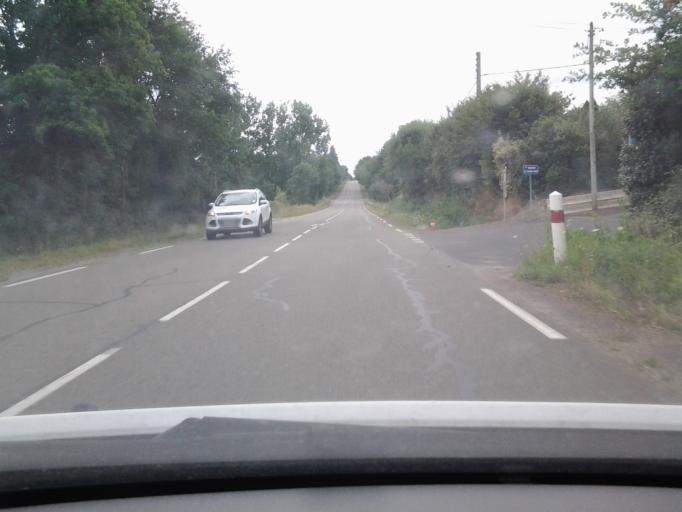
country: FR
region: Pays de la Loire
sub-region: Departement de la Vendee
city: Les Clouzeaux
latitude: 46.6583
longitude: -1.4768
